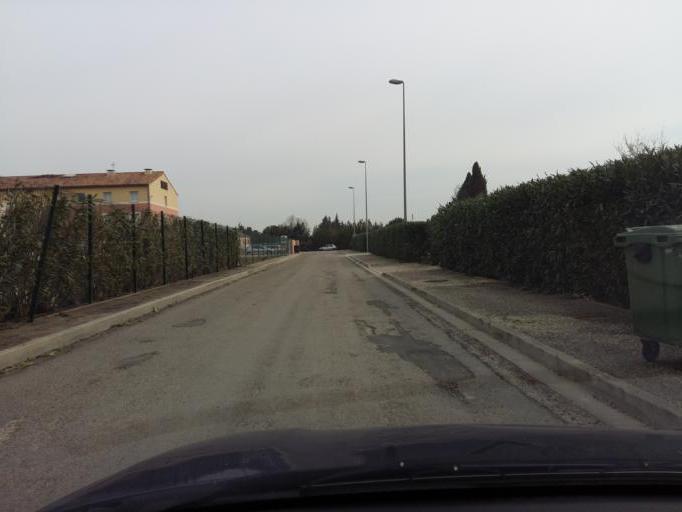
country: FR
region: Provence-Alpes-Cote d'Azur
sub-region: Departement des Bouches-du-Rhone
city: Chateaurenard
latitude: 43.8854
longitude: 4.8686
